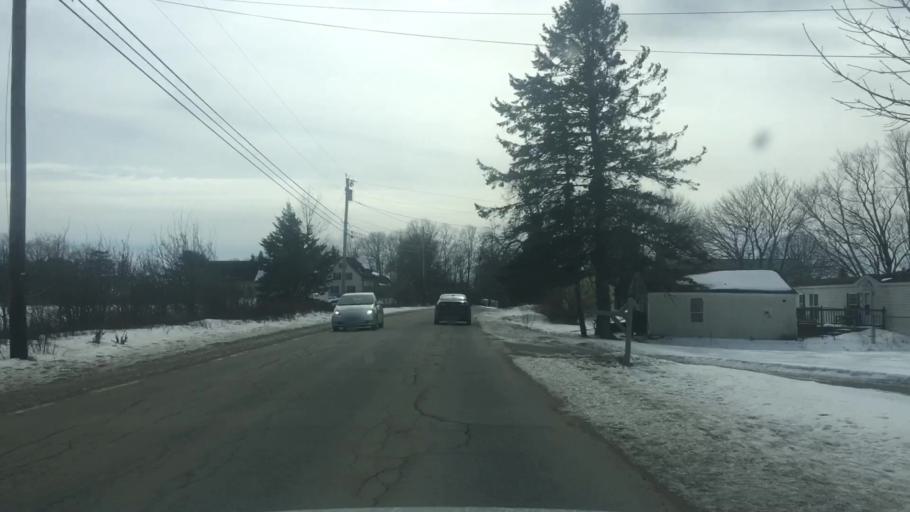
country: US
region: Maine
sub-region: Hancock County
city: Orland
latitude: 44.5788
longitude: -68.7255
